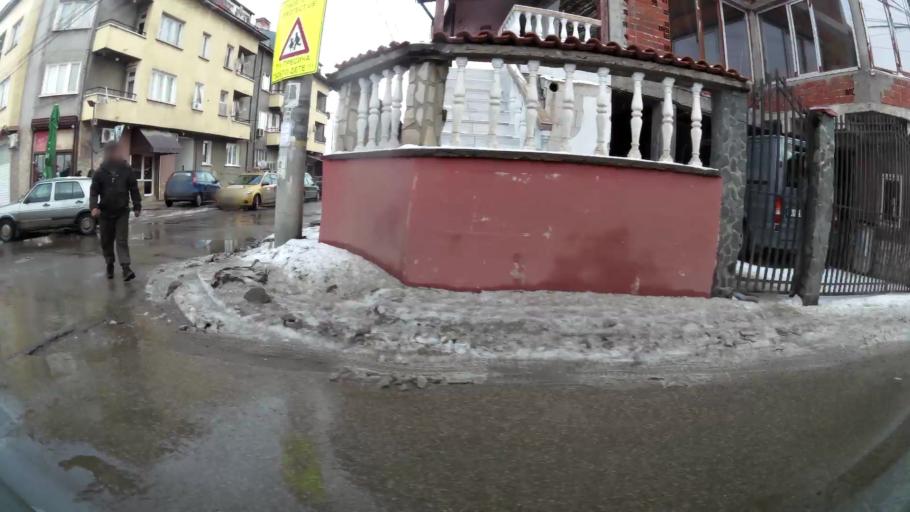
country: BG
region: Sofia-Capital
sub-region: Stolichna Obshtina
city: Sofia
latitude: 42.6898
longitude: 23.3809
